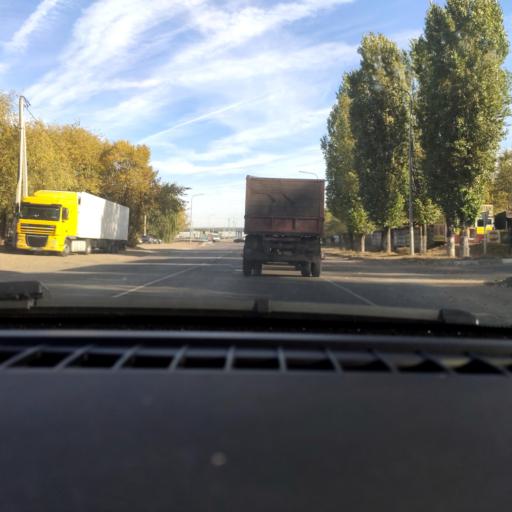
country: RU
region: Voronezj
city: Maslovka
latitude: 51.6448
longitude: 39.2968
